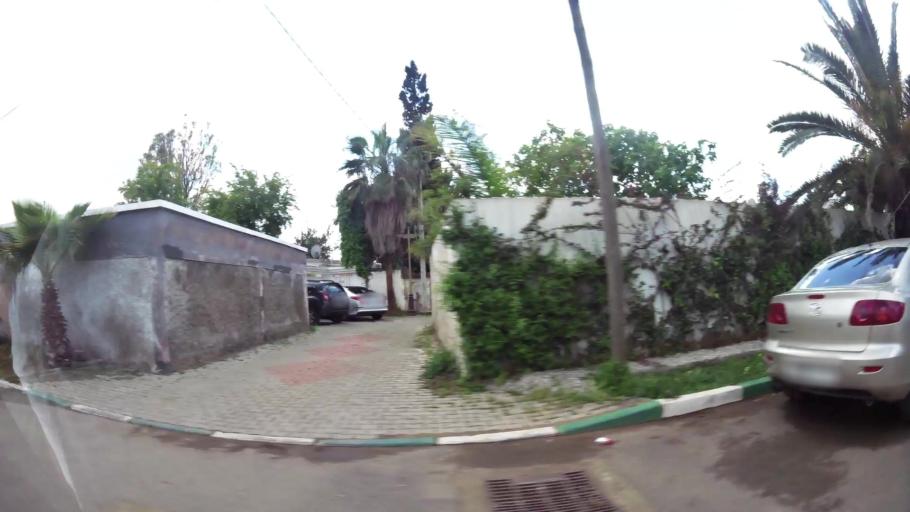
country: MA
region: Grand Casablanca
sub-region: Mediouna
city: Mediouna
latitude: 33.3836
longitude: -7.5400
